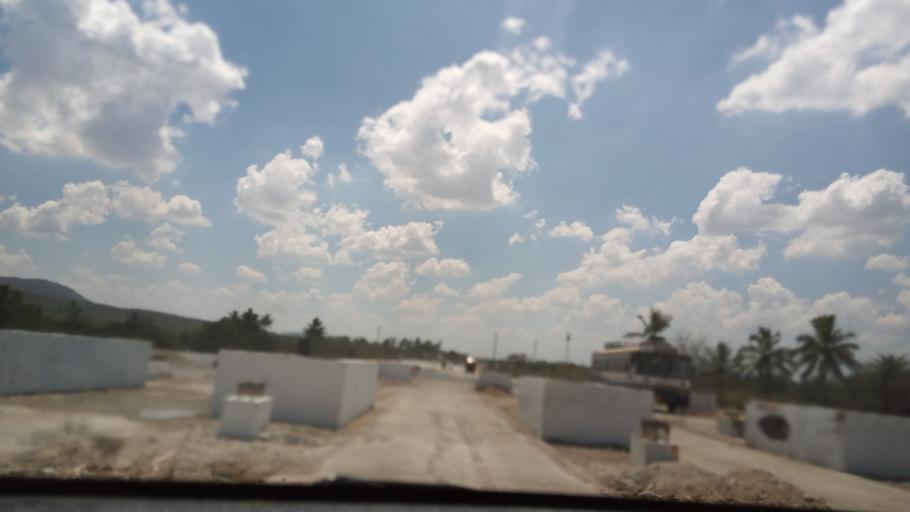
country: IN
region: Andhra Pradesh
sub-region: Chittoor
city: Pakala
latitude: 13.4781
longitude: 79.1878
